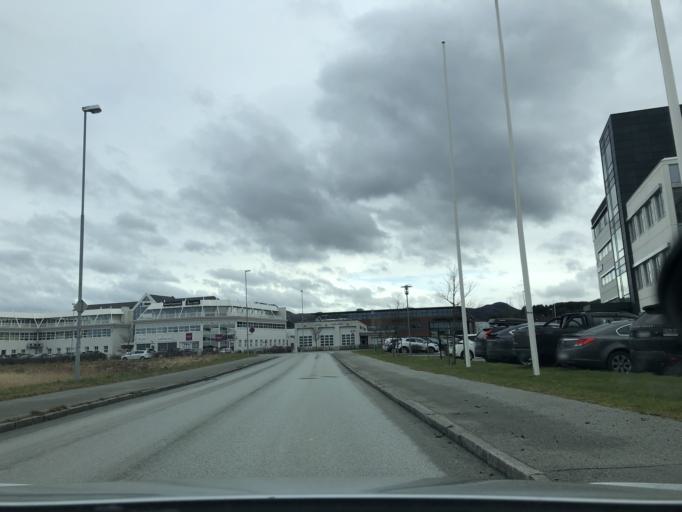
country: NO
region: Rogaland
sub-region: Sandnes
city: Sandnes
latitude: 58.8850
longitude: 5.7232
